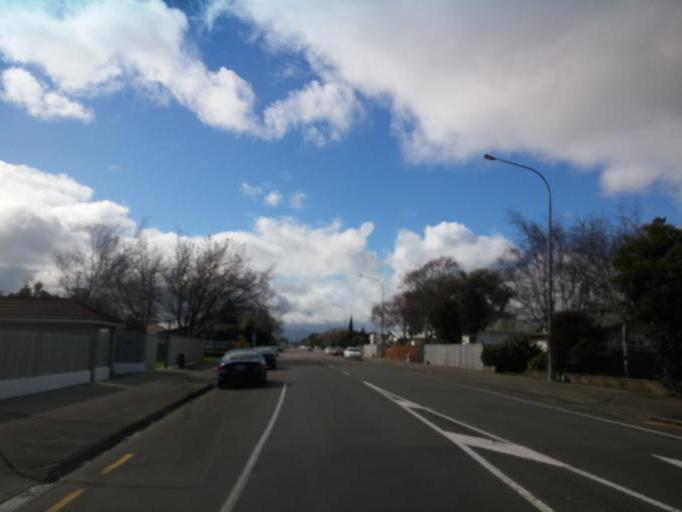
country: NZ
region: Manawatu-Wanganui
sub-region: Palmerston North City
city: Palmerston North
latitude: -40.3668
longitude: 175.5972
